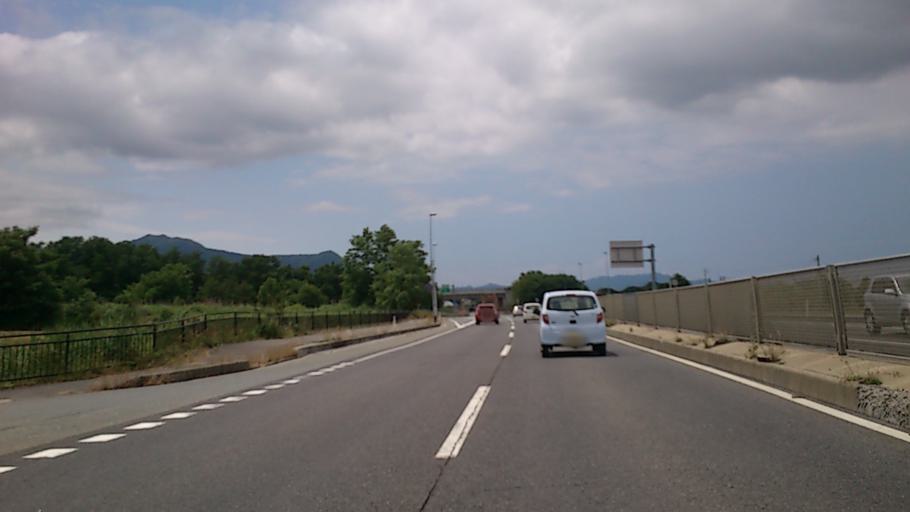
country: JP
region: Yamagata
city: Kaminoyama
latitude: 38.1906
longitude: 140.3113
